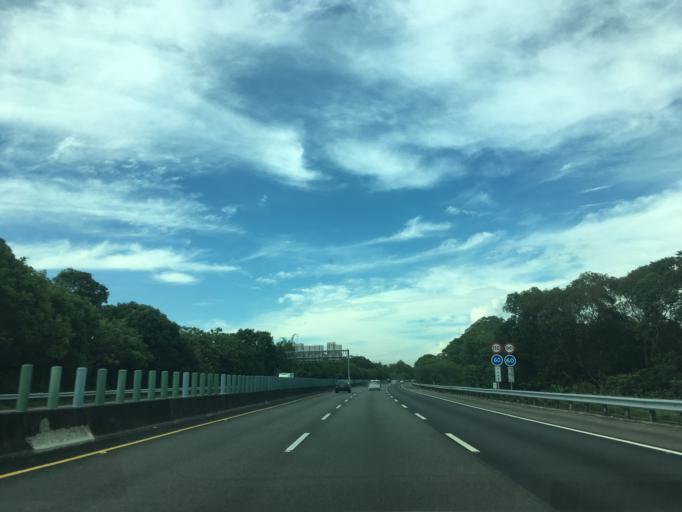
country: TW
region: Taiwan
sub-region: Chiayi
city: Jiayi Shi
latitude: 23.5308
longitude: 120.4880
